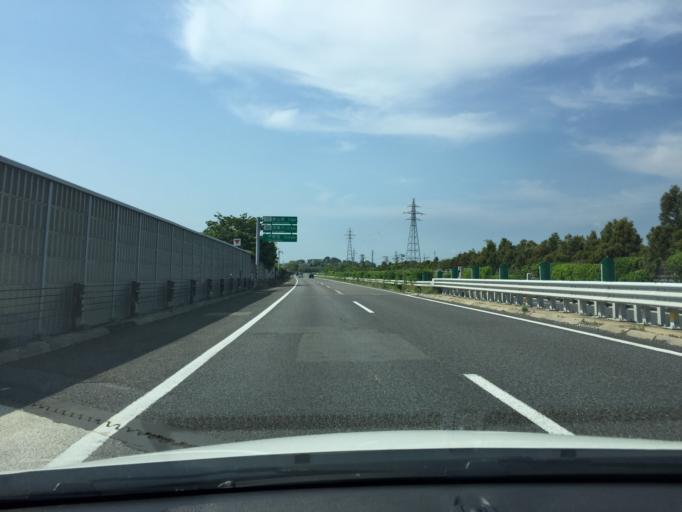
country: JP
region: Fukushima
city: Koriyama
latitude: 37.4243
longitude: 140.3345
